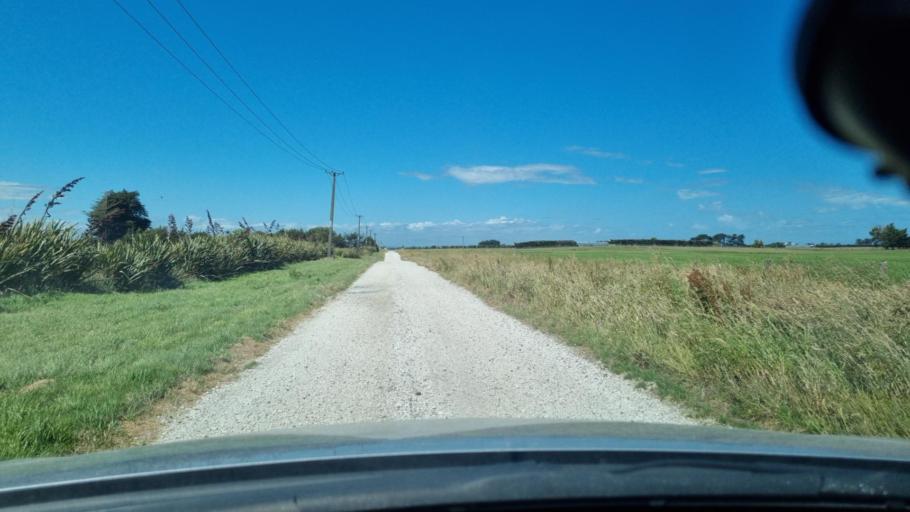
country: NZ
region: Southland
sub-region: Invercargill City
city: Invercargill
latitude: -46.4427
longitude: 168.4543
